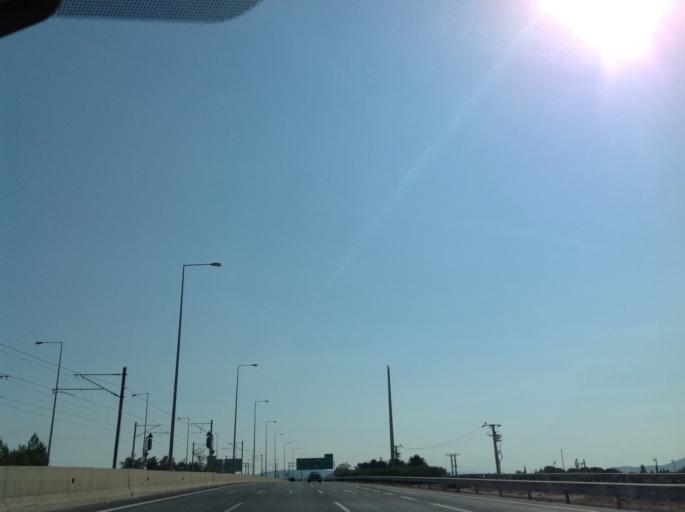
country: GR
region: Attica
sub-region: Nomarchia Anatolikis Attikis
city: Markopoulo
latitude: 37.9107
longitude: 23.9079
